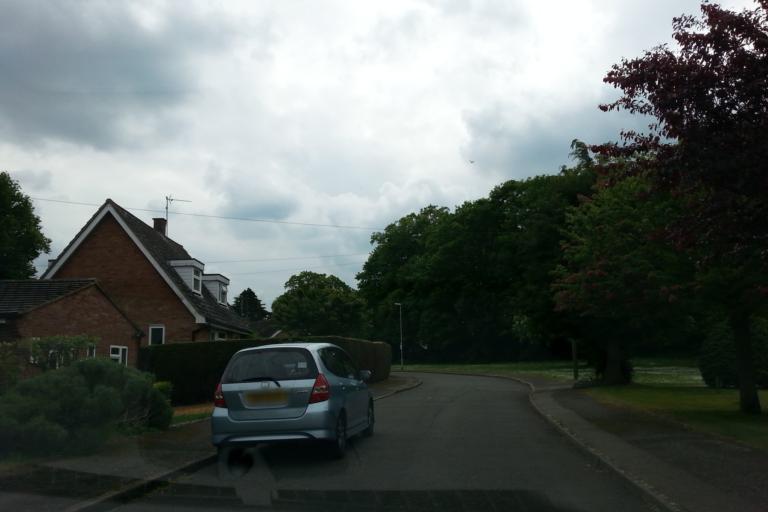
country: GB
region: England
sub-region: Cambridgeshire
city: Girton
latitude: 52.2790
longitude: 0.0501
